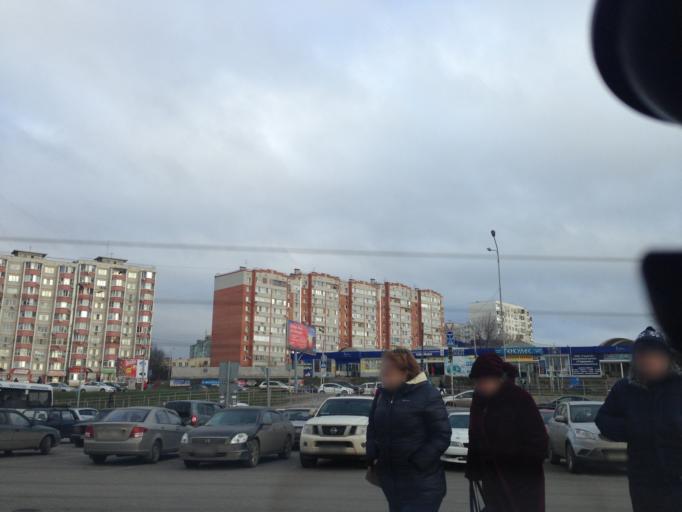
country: RU
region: Rostov
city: Temernik
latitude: 47.2933
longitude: 39.7338
